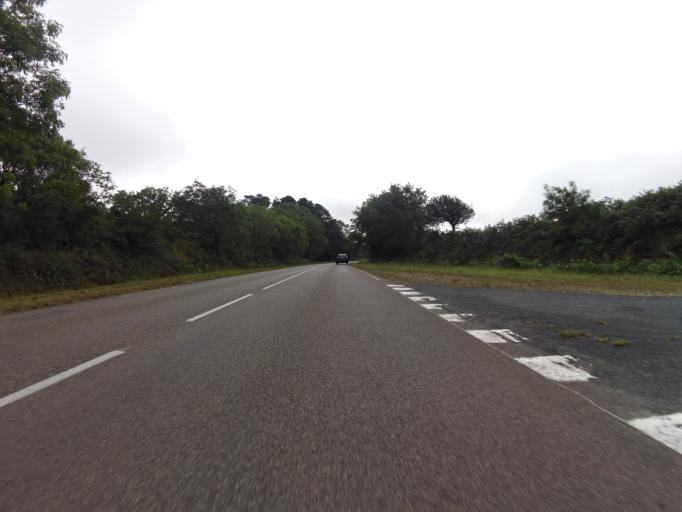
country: FR
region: Brittany
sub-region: Departement du Finistere
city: Plouhinec
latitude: 48.0120
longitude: -4.4708
